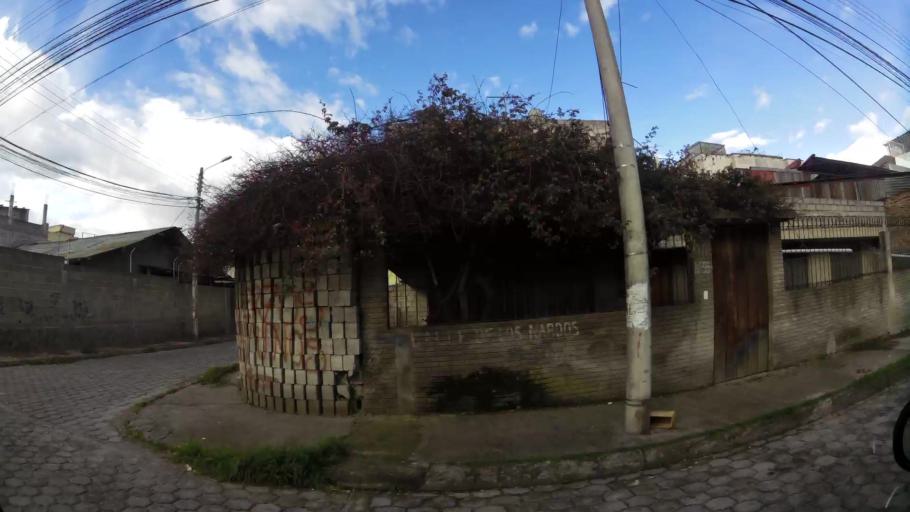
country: EC
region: Pichincha
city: Quito
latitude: -0.1323
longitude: -78.4700
